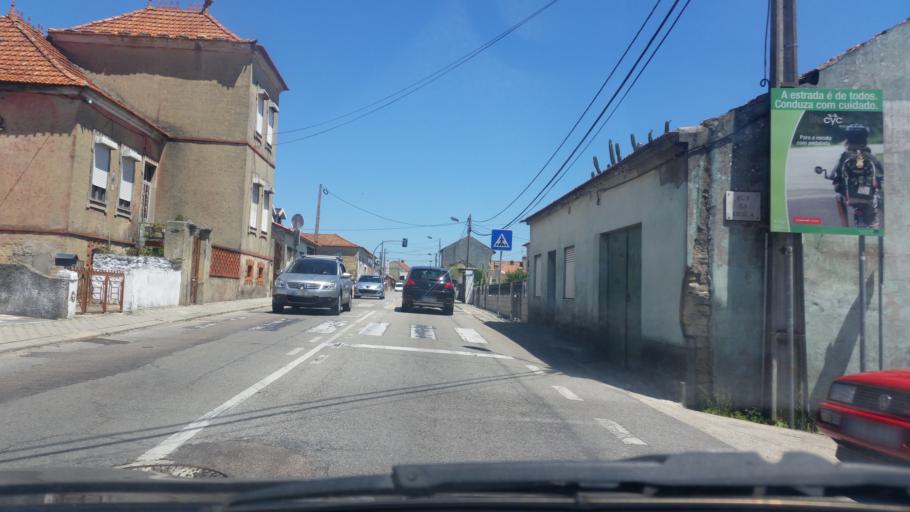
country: PT
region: Aveiro
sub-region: Aveiro
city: Eixo
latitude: 40.6376
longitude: -8.5934
